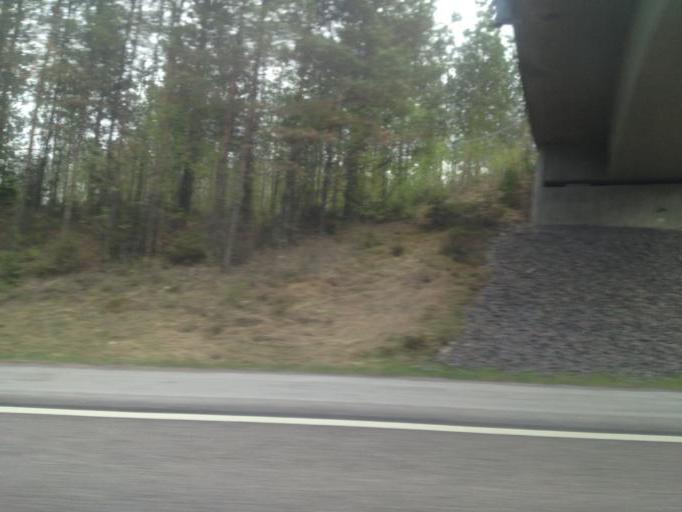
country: FI
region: Uusimaa
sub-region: Helsinki
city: Hyvinge
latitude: 60.6426
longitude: 24.8084
